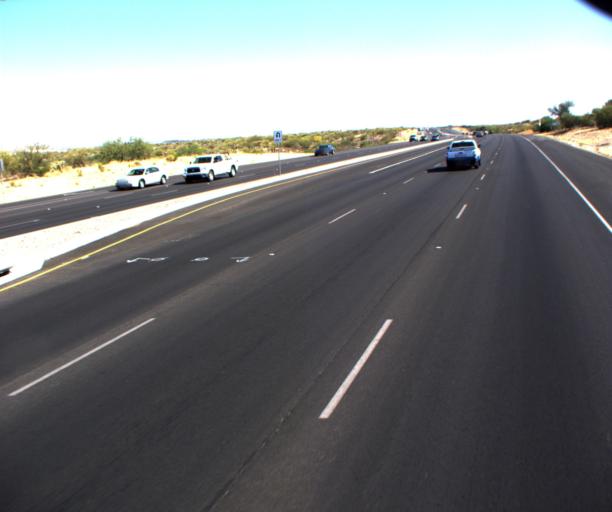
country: US
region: Arizona
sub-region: Pima County
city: Oro Valley
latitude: 32.4281
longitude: -110.9344
